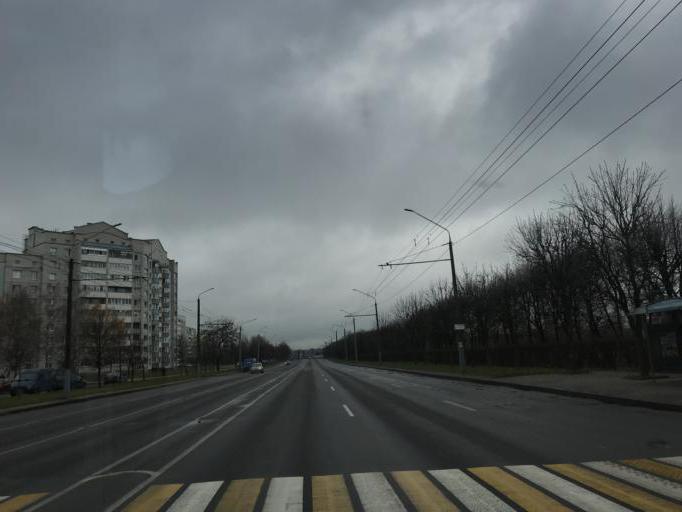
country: BY
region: Mogilev
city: Mahilyow
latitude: 53.8659
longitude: 30.3308
